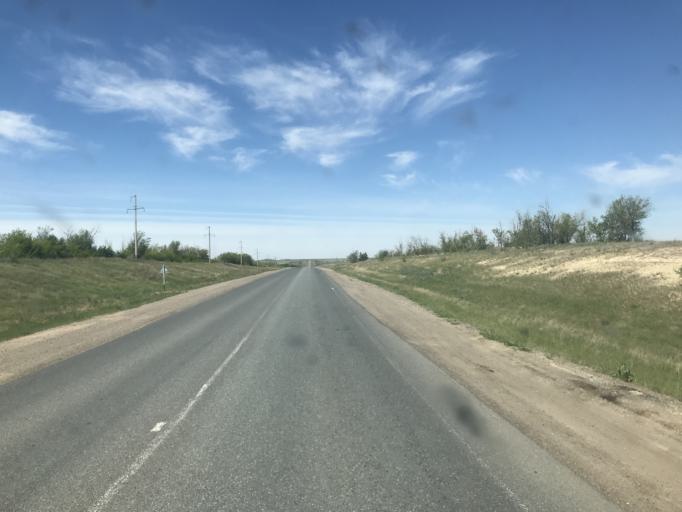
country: KZ
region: Aqtoebe
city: Aqtobe
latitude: 50.2369
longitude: 56.6755
